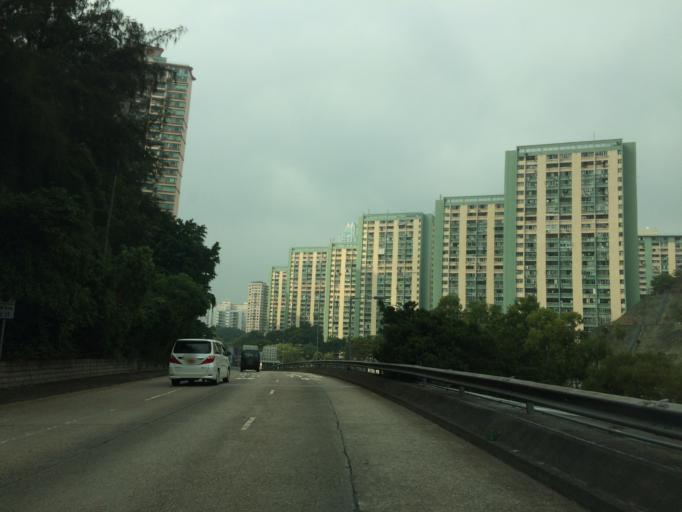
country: HK
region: Kowloon City
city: Kowloon
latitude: 22.3090
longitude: 114.1788
